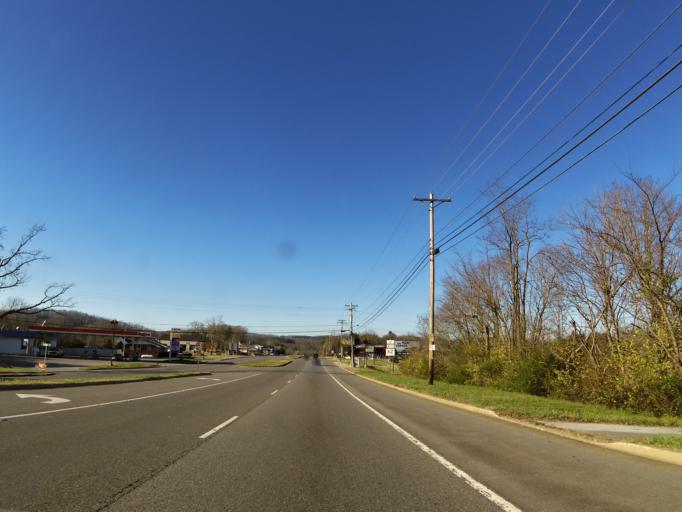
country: US
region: Tennessee
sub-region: Anderson County
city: Oak Ridge
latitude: 35.9822
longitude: -84.1833
